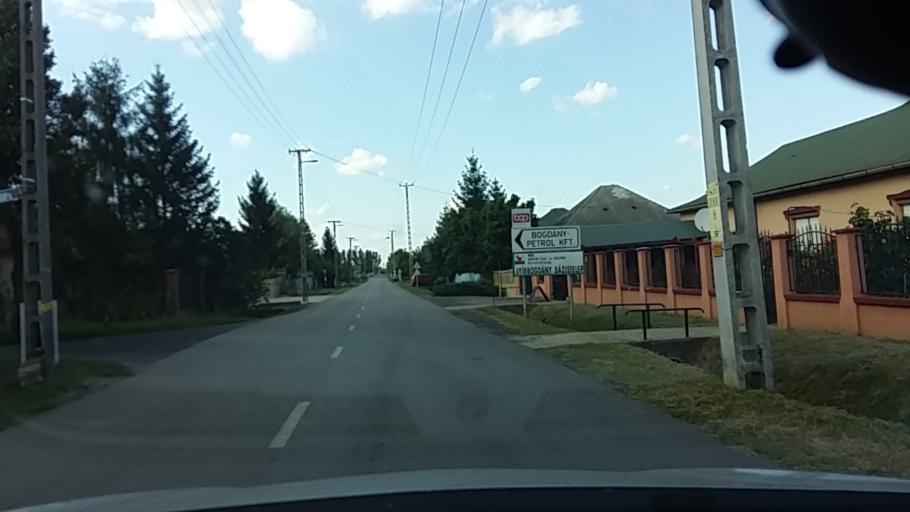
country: HU
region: Szabolcs-Szatmar-Bereg
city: Nyirbogdany
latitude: 48.0804
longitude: 21.8581
